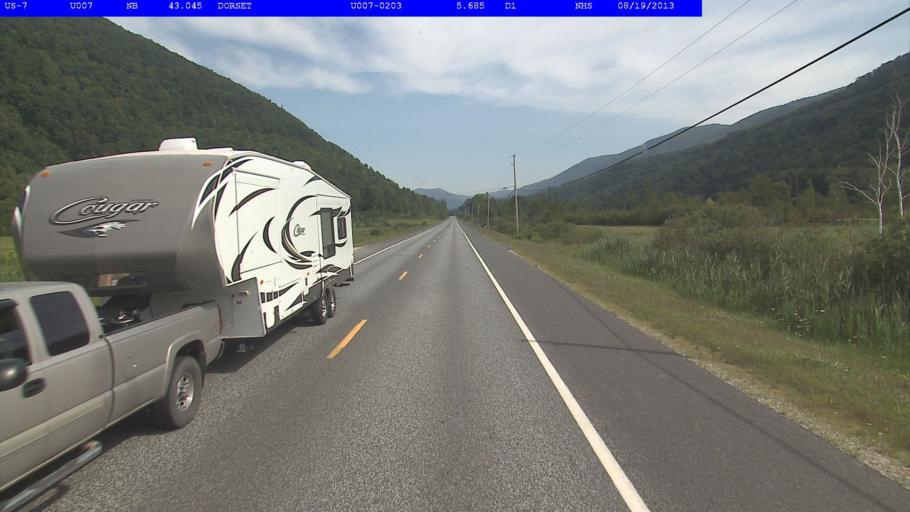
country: US
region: Vermont
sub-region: Bennington County
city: Manchester Center
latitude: 43.2904
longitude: -72.9997
